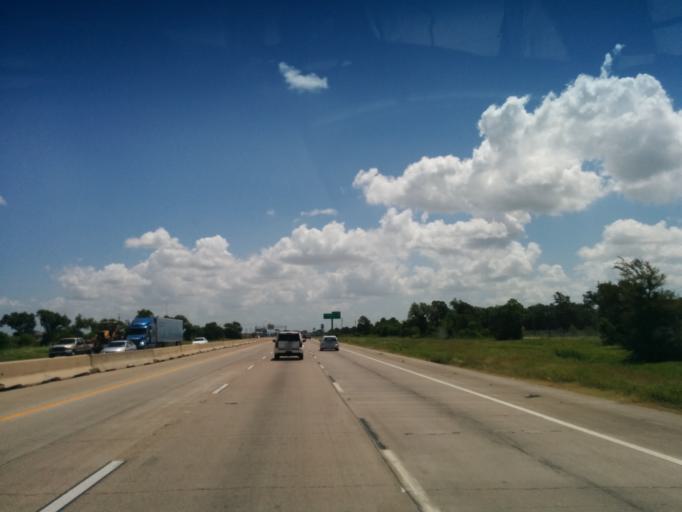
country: US
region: Texas
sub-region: Harris County
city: Highlands
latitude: 29.7925
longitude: -95.0453
